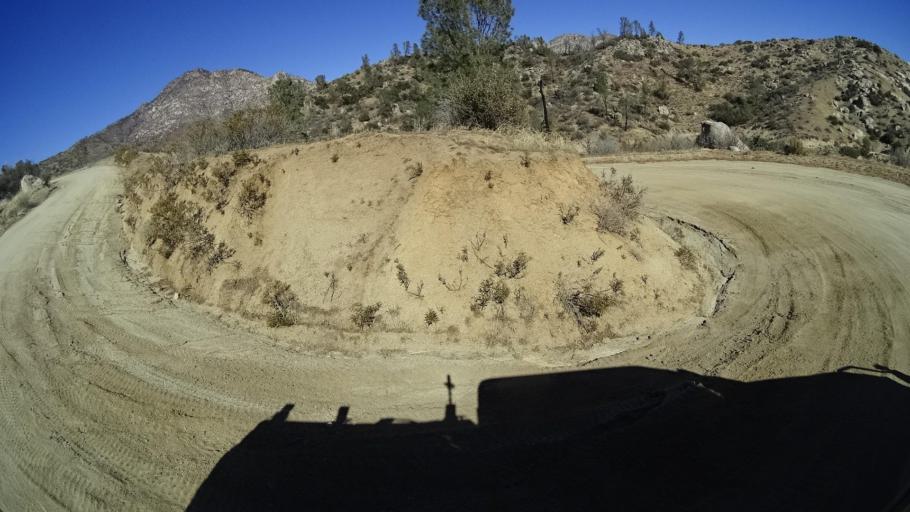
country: US
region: California
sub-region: Kern County
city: Wofford Heights
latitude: 35.7045
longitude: -118.4984
